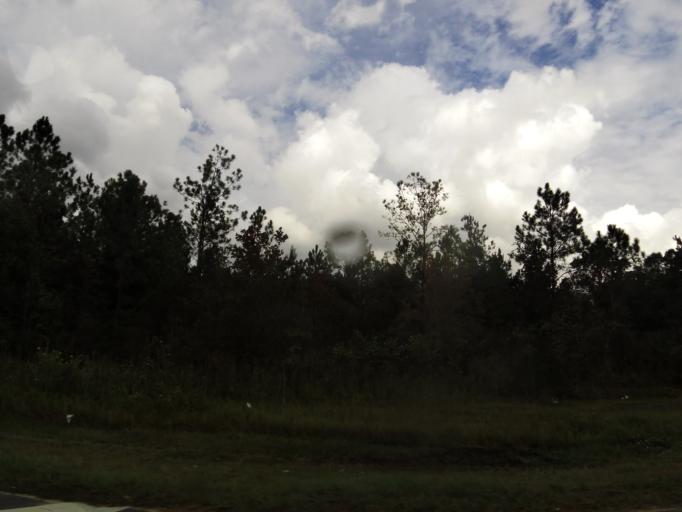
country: US
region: Florida
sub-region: Clay County
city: Middleburg
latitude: 30.0630
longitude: -81.8792
